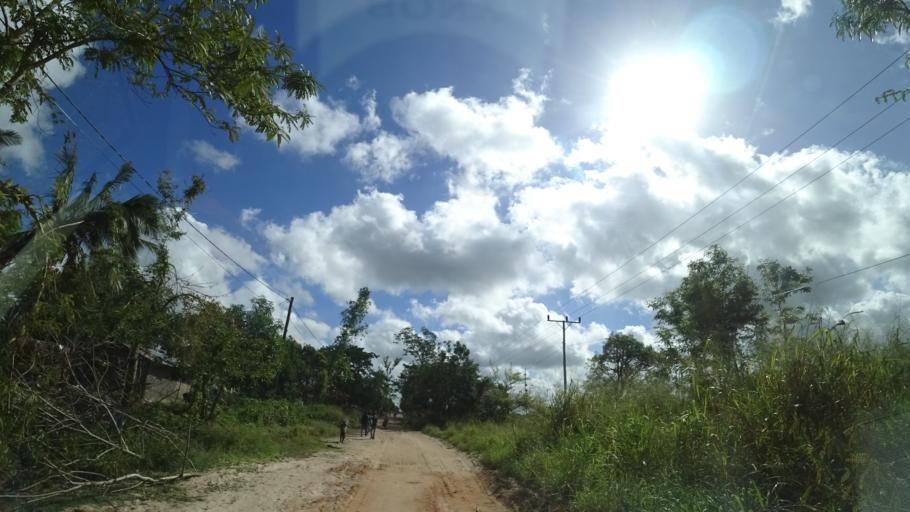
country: MZ
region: Sofala
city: Dondo
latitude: -19.3893
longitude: 34.7084
